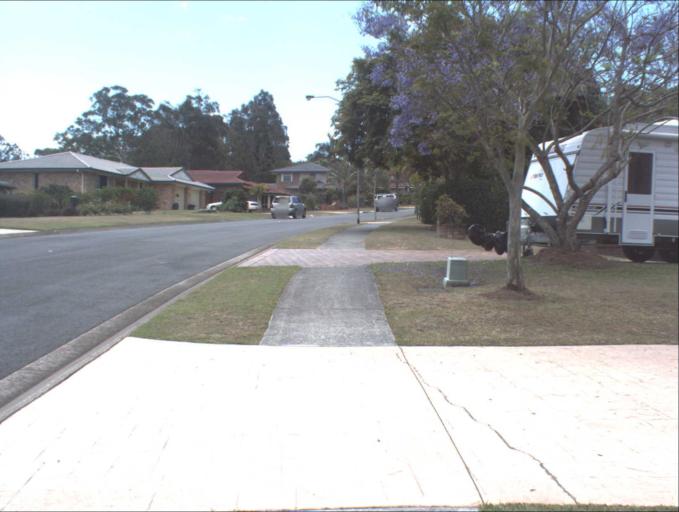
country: AU
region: Queensland
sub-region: Logan
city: Slacks Creek
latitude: -27.6418
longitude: 153.1810
